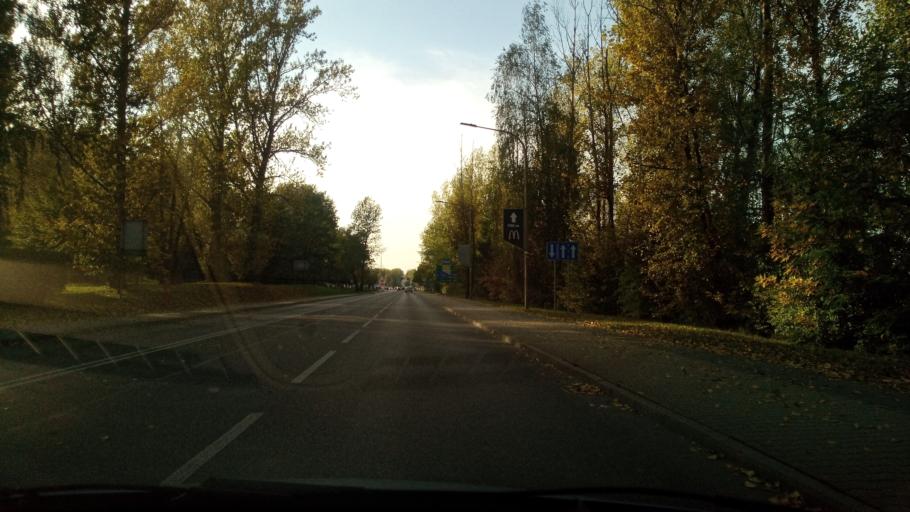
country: PL
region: Silesian Voivodeship
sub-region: Sosnowiec
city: Sosnowiec
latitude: 50.2477
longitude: 19.1229
